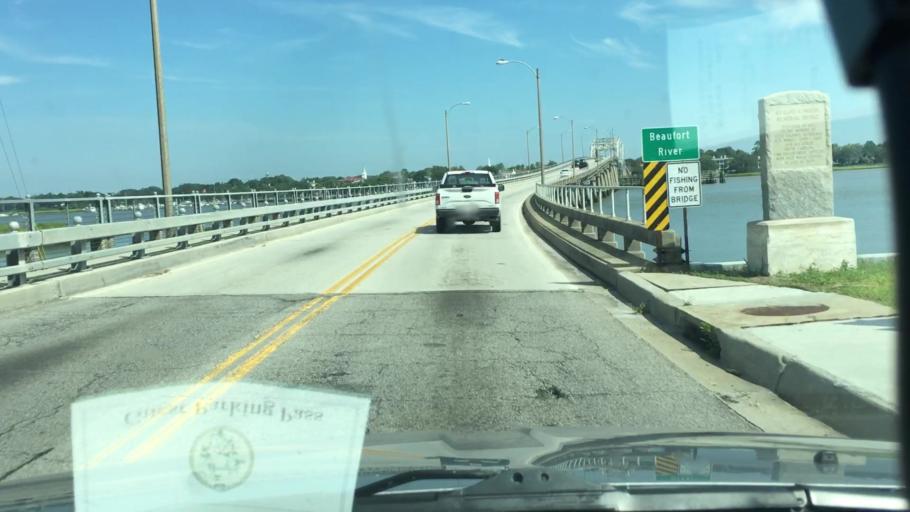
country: US
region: South Carolina
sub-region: Beaufort County
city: Beaufort
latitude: 32.4241
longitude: -80.6681
